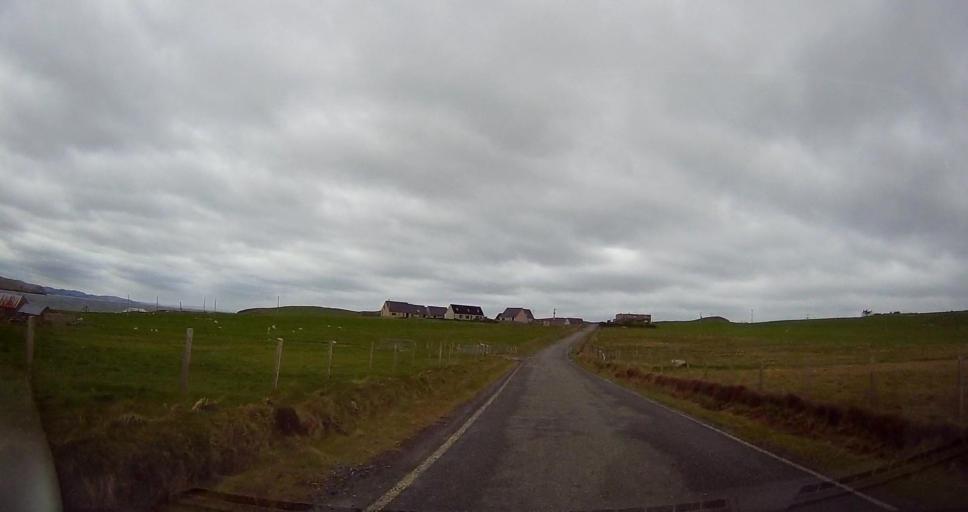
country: GB
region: Scotland
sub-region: Shetland Islands
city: Lerwick
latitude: 60.4809
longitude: -1.4774
